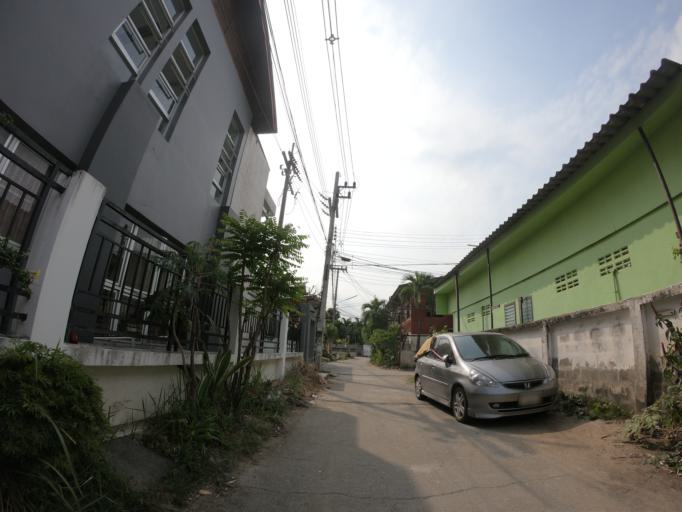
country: TH
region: Chiang Mai
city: Chiang Mai
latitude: 18.7571
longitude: 98.9704
